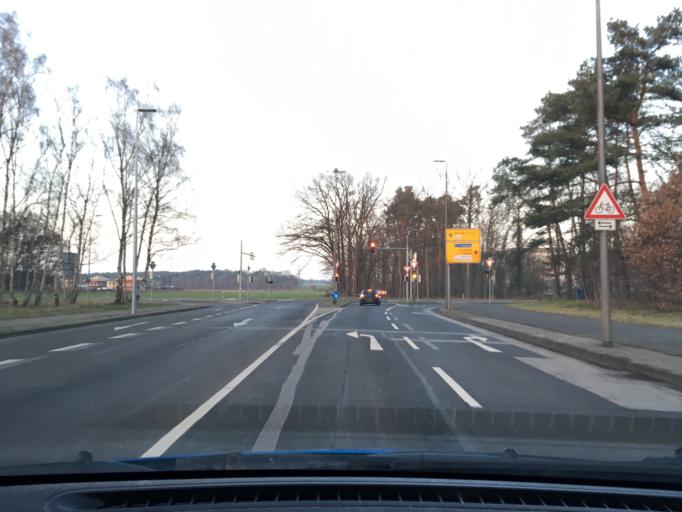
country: DE
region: Lower Saxony
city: Celle
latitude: 52.6373
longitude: 10.0478
